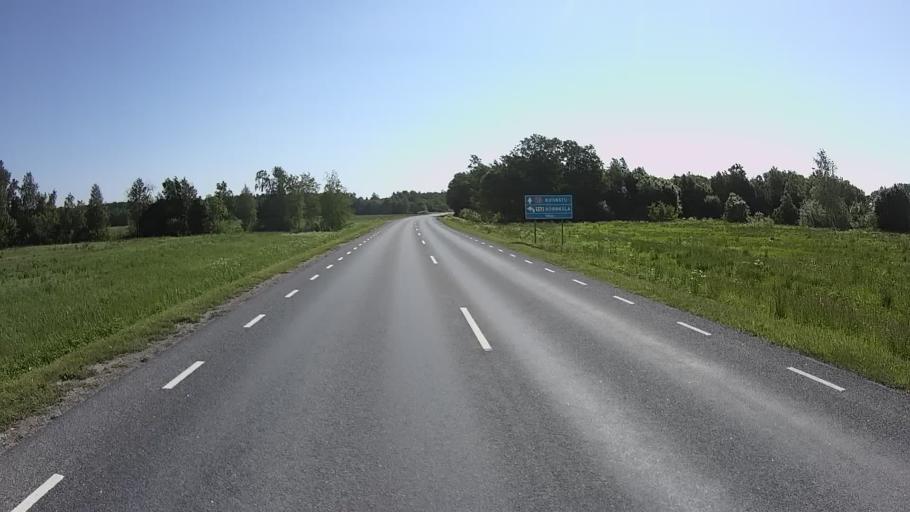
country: EE
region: Saare
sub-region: Orissaare vald
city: Orissaare
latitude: 58.6084
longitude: 23.2739
